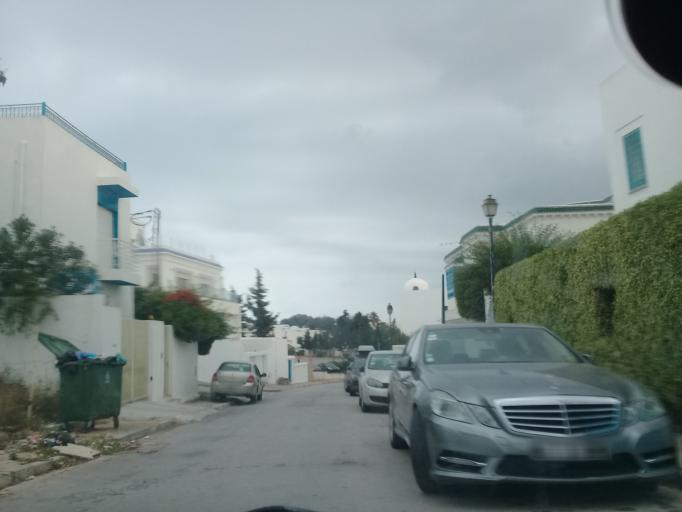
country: TN
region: Tunis
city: Sidi Bou Said
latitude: 36.8724
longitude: 10.3420
